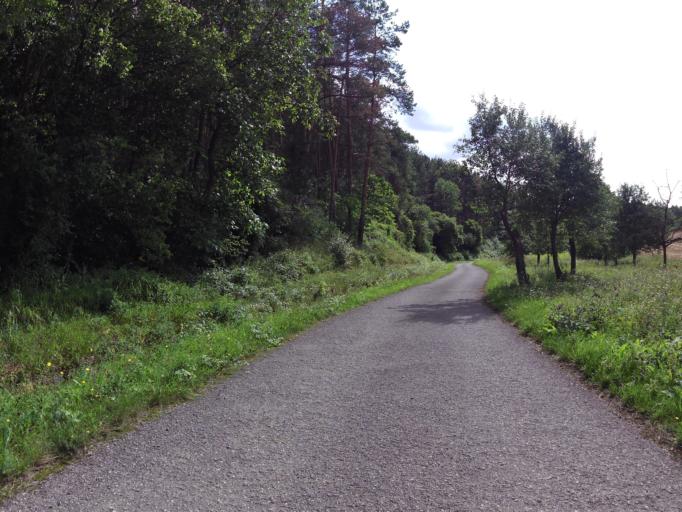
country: DE
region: Bavaria
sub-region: Regierungsbezirk Unterfranken
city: Erlabrunn
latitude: 49.8439
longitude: 9.8440
